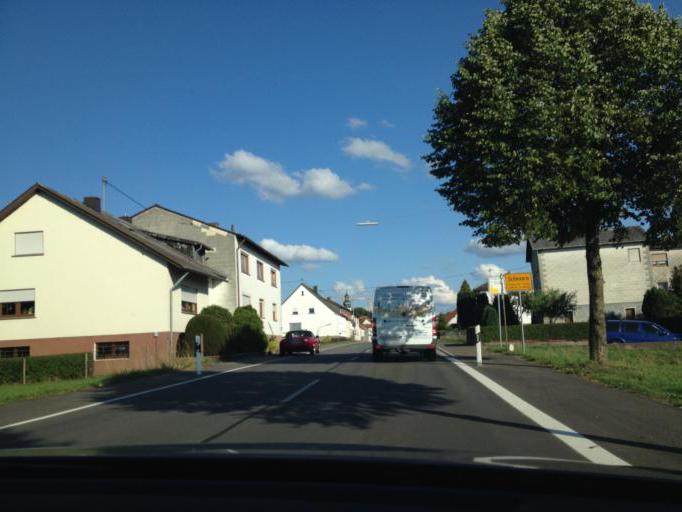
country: DE
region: Saarland
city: Wadern
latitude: 49.4868
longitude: 6.9348
